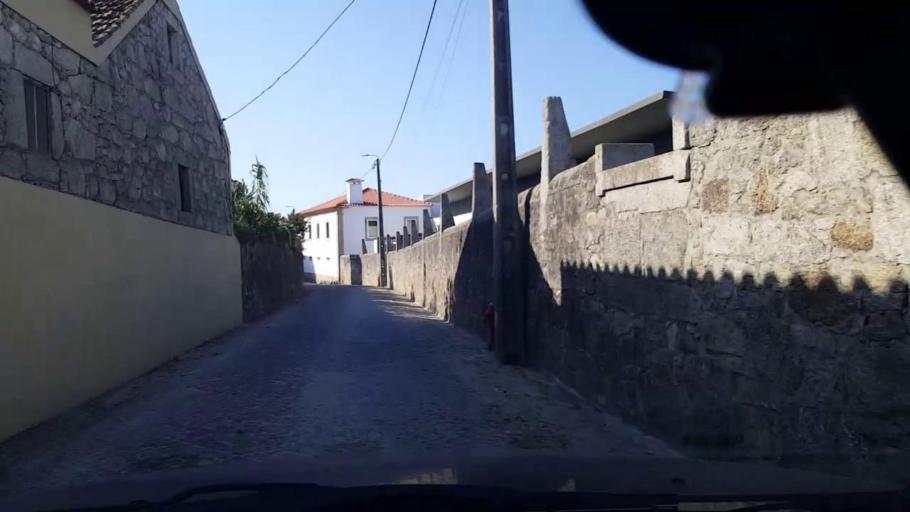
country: PT
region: Porto
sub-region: Vila do Conde
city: Arvore
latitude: 41.3569
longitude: -8.7178
